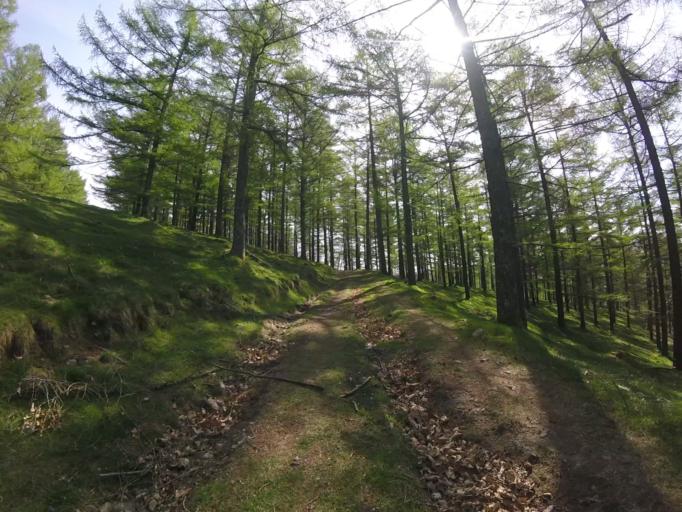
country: ES
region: Navarre
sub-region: Provincia de Navarra
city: Arano
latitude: 43.2552
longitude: -1.8303
